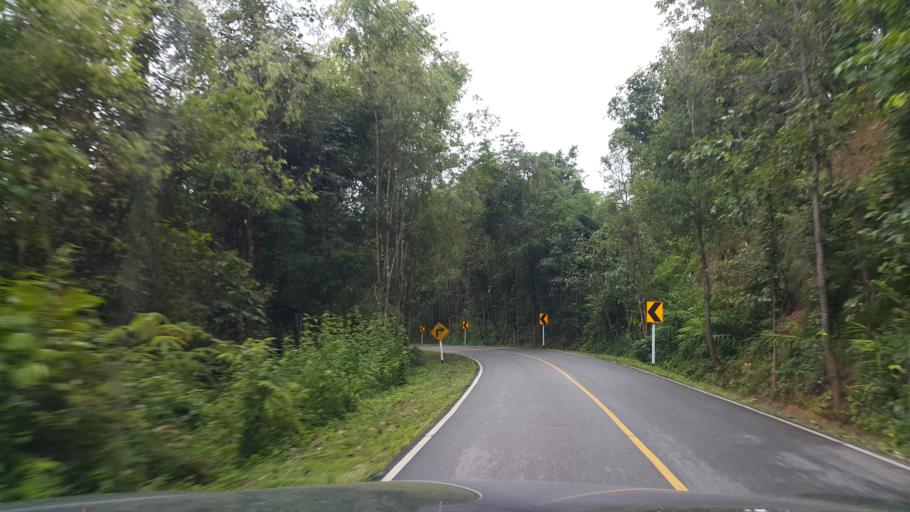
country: TH
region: Chiang Mai
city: Samoeng
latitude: 18.8591
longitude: 98.6607
